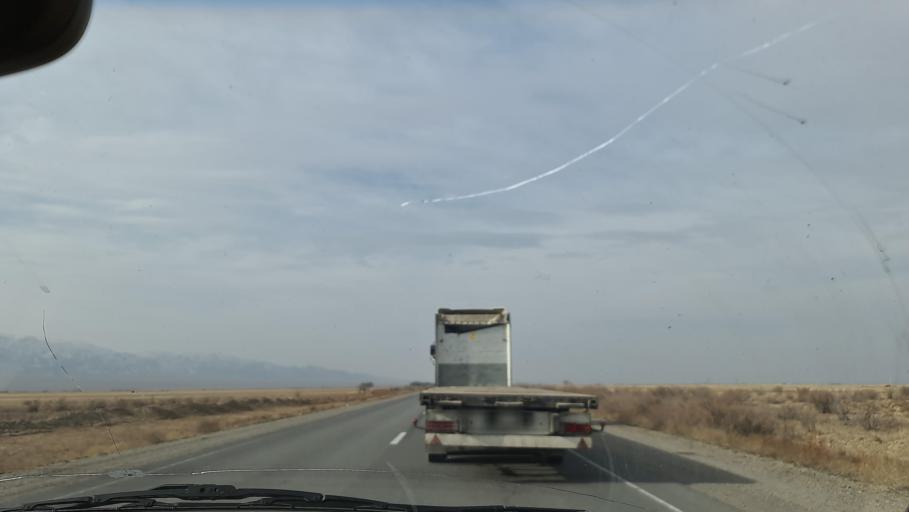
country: KG
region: Chuy
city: Tokmok
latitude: 43.3465
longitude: 75.5060
